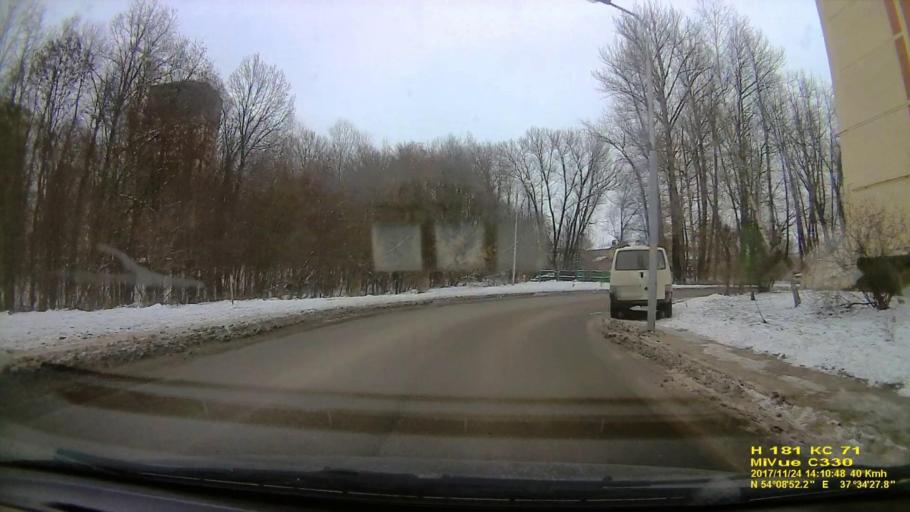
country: RU
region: Tula
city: Mendeleyevskiy
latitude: 54.1475
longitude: 37.5748
